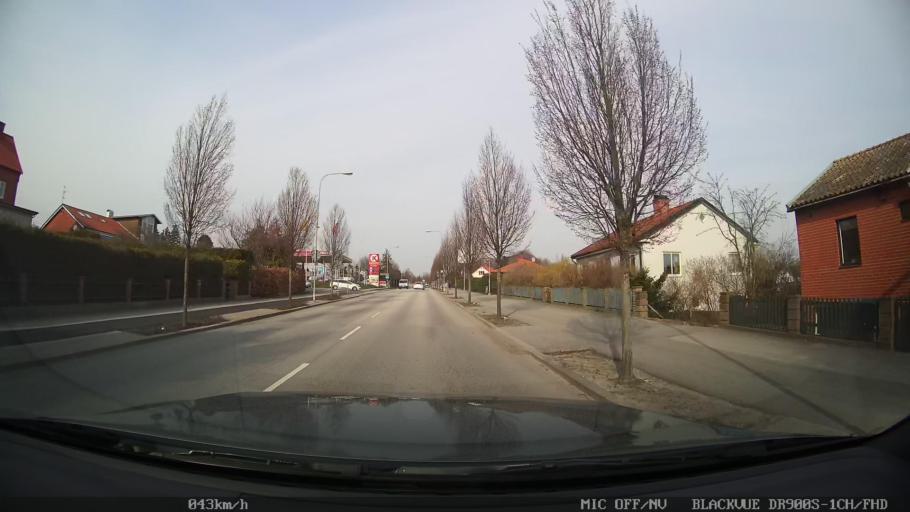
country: SE
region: Skane
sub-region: Ystads Kommun
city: Ystad
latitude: 55.4354
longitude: 13.8225
